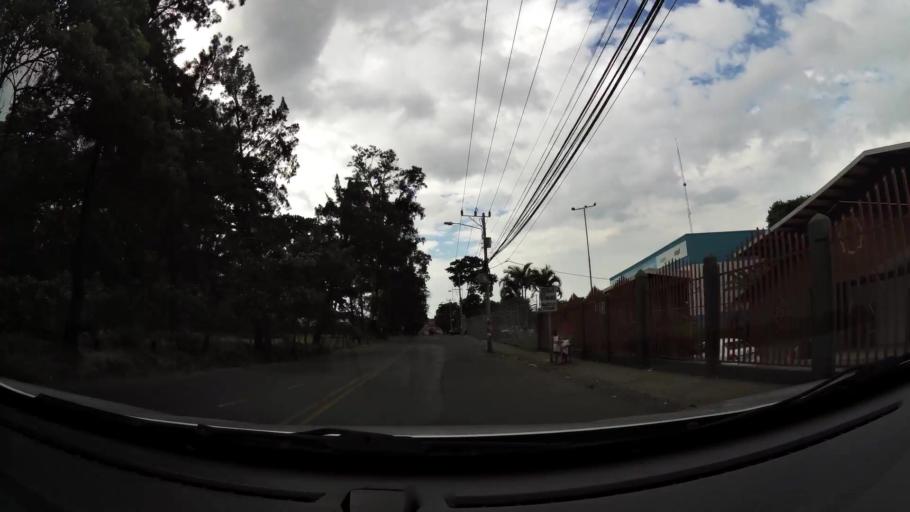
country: CR
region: San Jose
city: San Felipe
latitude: 9.9146
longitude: -84.1144
